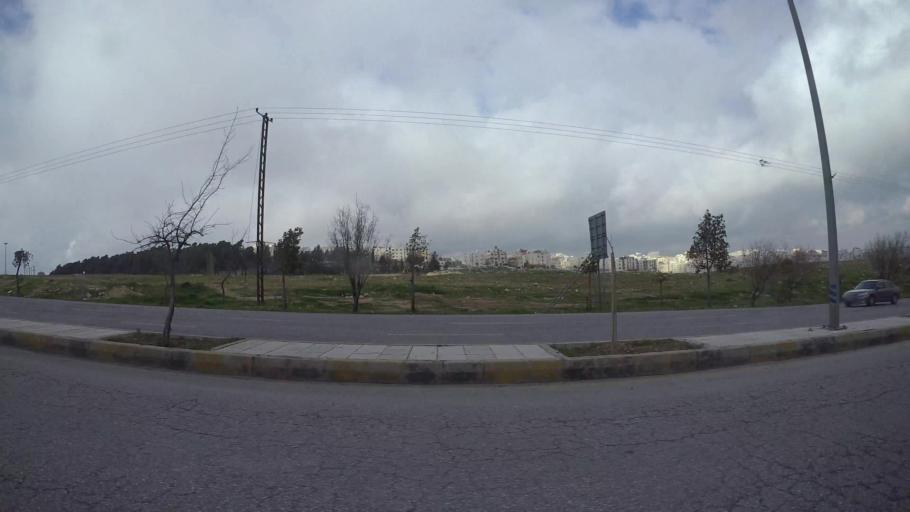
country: JO
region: Amman
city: Al Jubayhah
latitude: 32.0430
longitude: 35.8736
